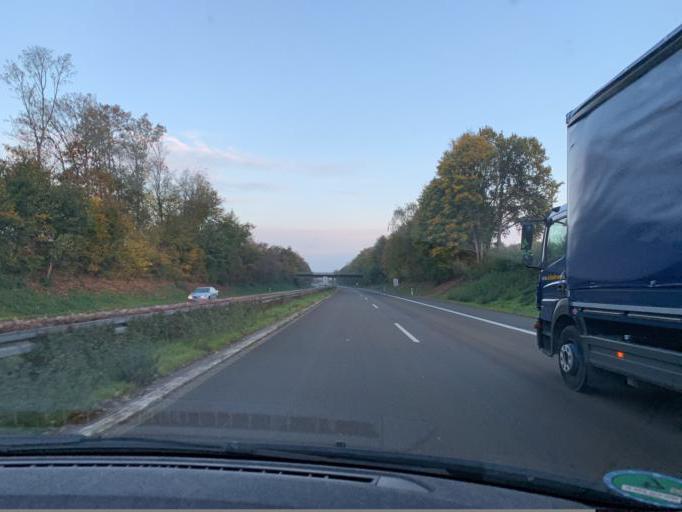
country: DE
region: North Rhine-Westphalia
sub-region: Regierungsbezirk Dusseldorf
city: Juchen
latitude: 51.1042
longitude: 6.4774
